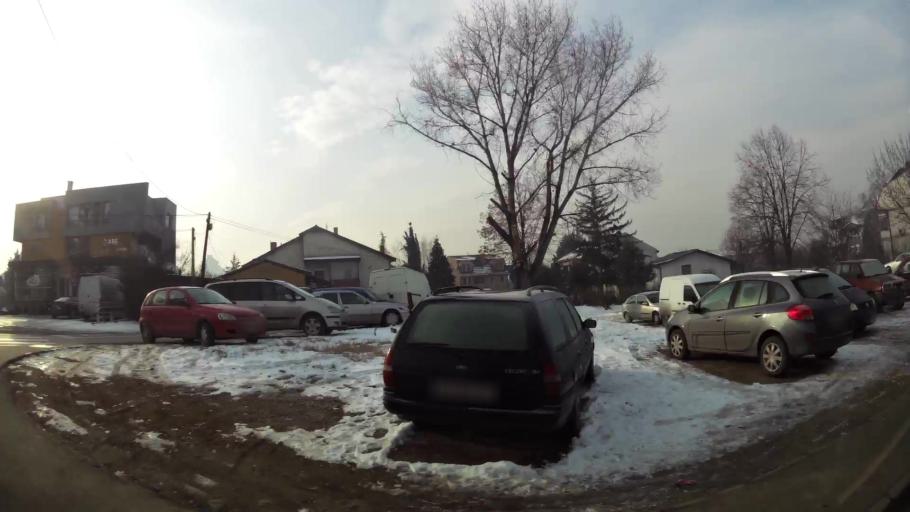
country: MK
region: Butel
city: Butel
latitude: 42.0208
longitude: 21.4506
